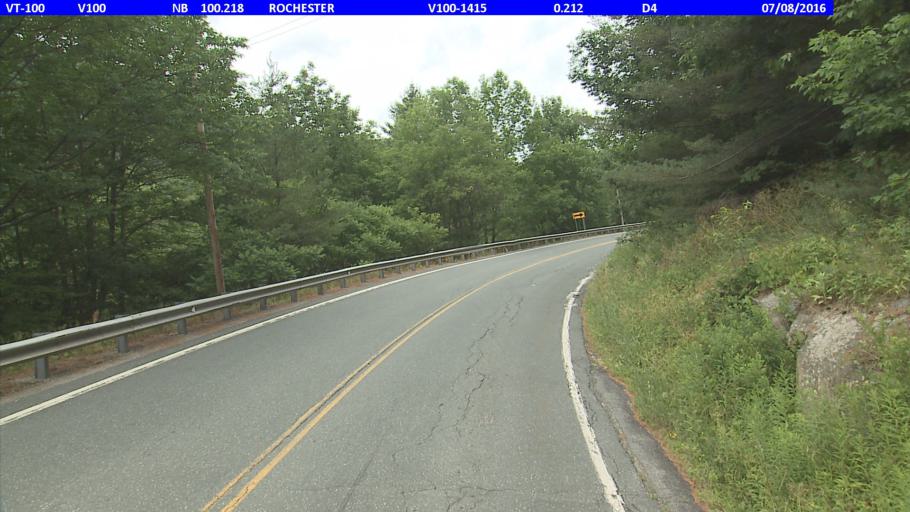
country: US
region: Vermont
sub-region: Orange County
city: Randolph
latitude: 43.8074
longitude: -72.7853
